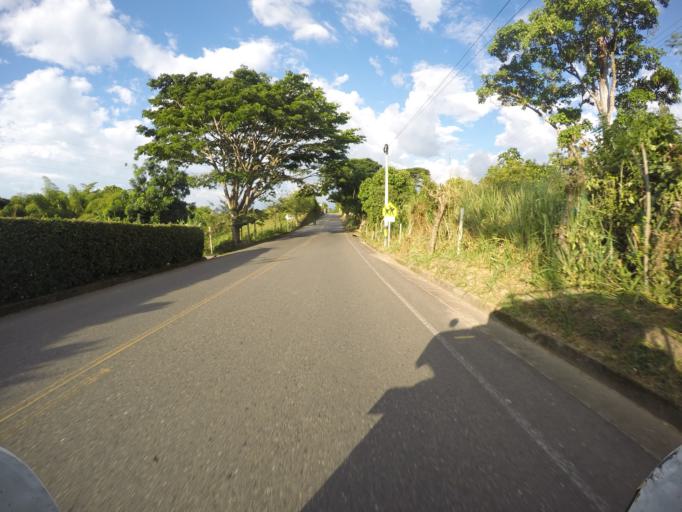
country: CO
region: Valle del Cauca
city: Alcala
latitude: 4.6811
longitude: -75.8060
